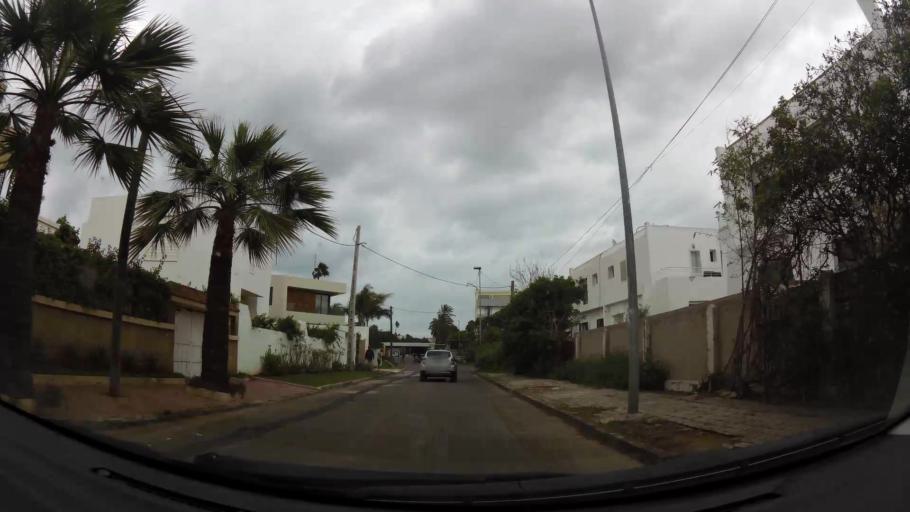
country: MA
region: Grand Casablanca
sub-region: Casablanca
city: Casablanca
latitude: 33.5939
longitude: -7.6584
